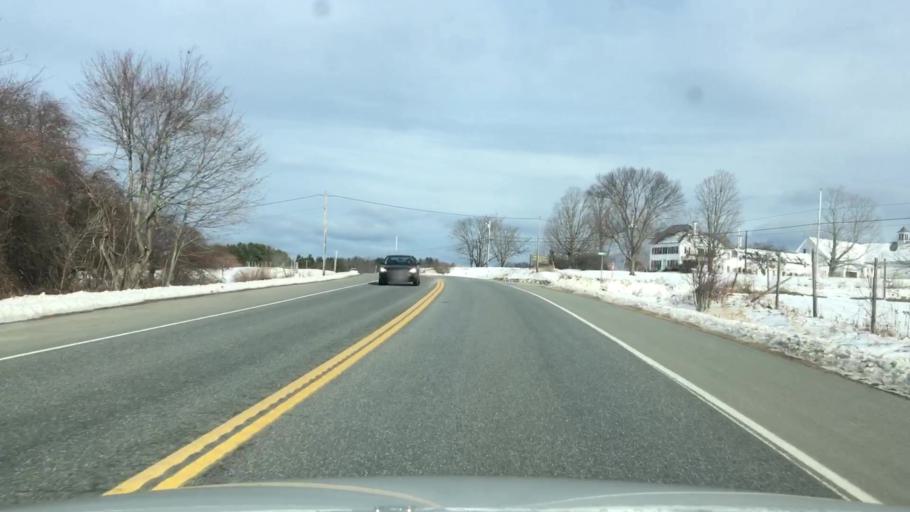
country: US
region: Maine
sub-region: Kennebec County
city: Monmouth
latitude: 44.2316
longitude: -70.0726
